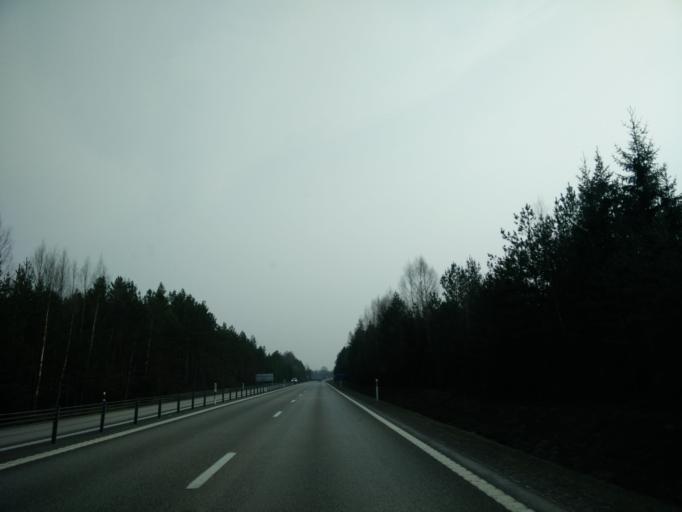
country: SE
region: Vaermland
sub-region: Forshaga Kommun
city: Forshaga
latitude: 59.4532
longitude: 13.4167
